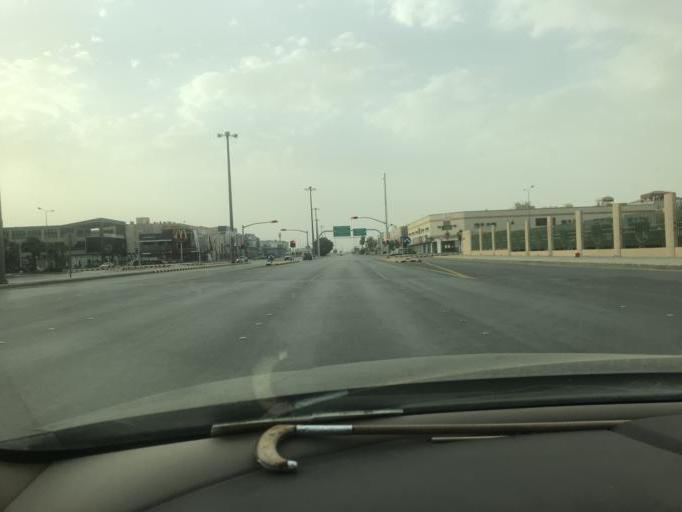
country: SA
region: Ar Riyad
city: Riyadh
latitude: 24.7928
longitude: 46.6571
